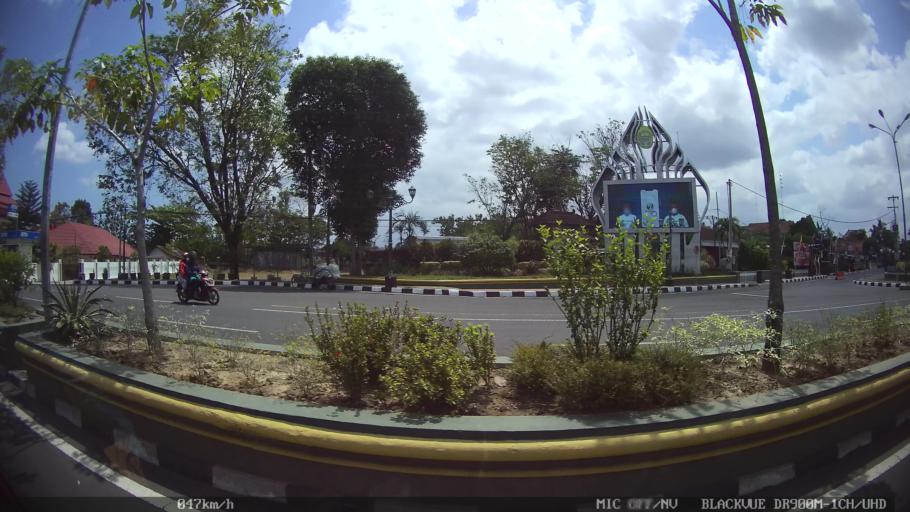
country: ID
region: Daerah Istimewa Yogyakarta
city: Bantul
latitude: -7.8893
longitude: 110.3264
